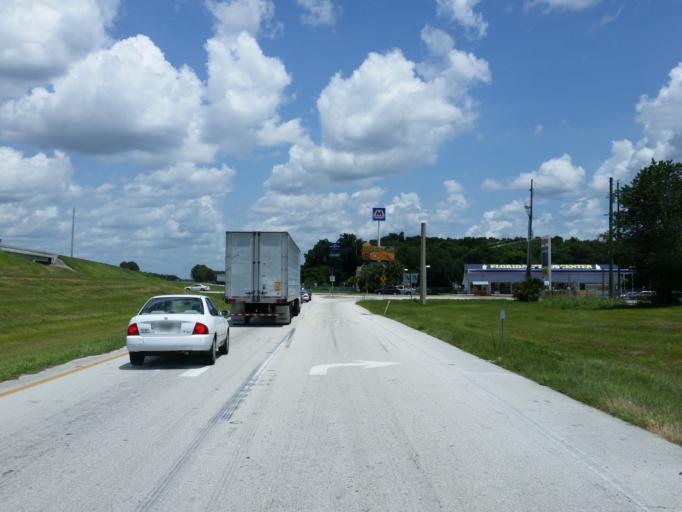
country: US
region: Florida
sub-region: Marion County
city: Belleview
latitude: 29.0243
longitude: -82.1566
